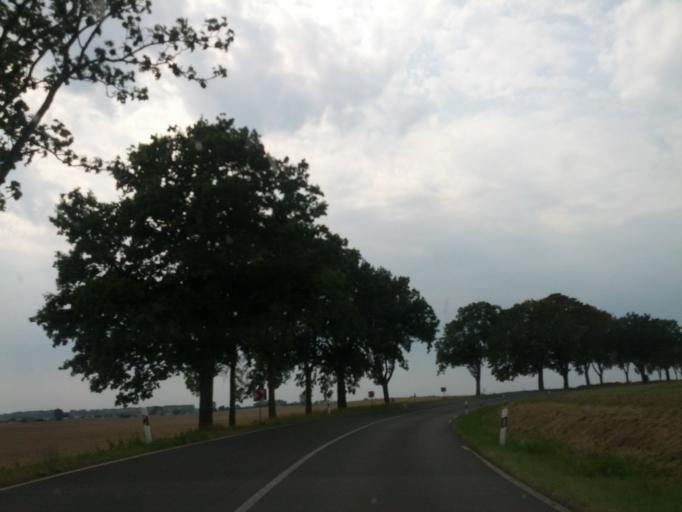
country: DE
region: Brandenburg
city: Kremmen
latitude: 52.7460
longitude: 12.9175
